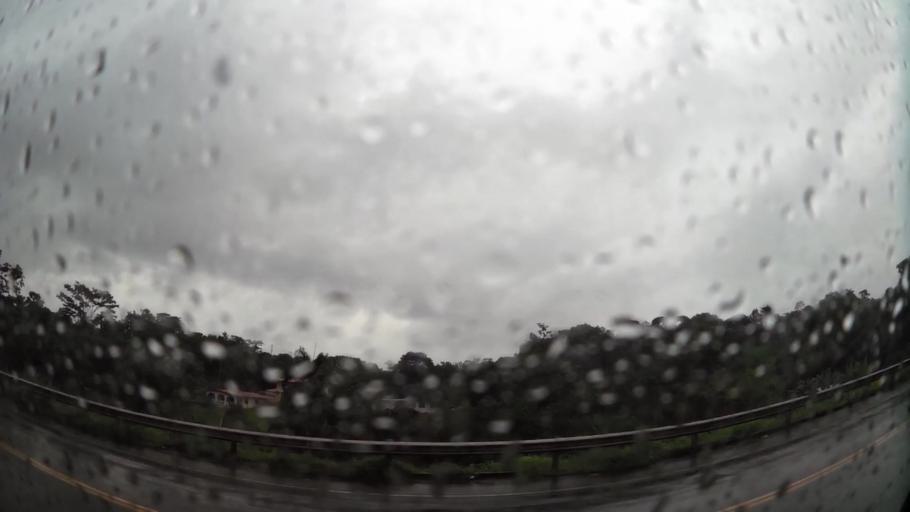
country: PA
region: Colon
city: Quebrada Bonita Adentro
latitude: 9.2860
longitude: -79.7170
